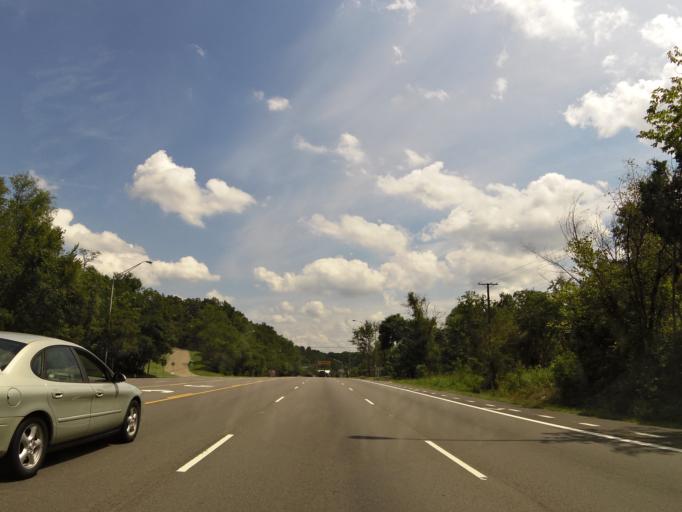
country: US
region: Tennessee
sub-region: Sullivan County
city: Kingsport
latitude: 36.5589
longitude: -82.5475
